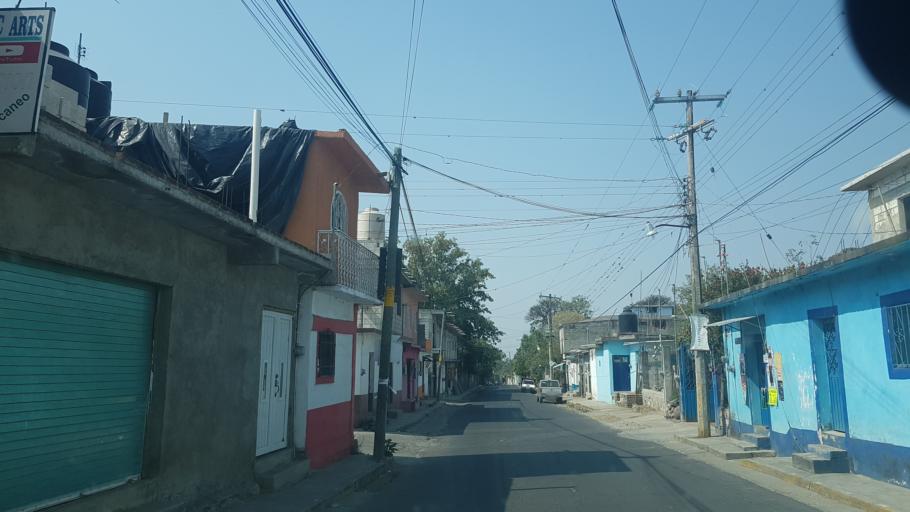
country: MX
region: Morelos
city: Tlacotepec
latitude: 18.8144
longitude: -98.7529
